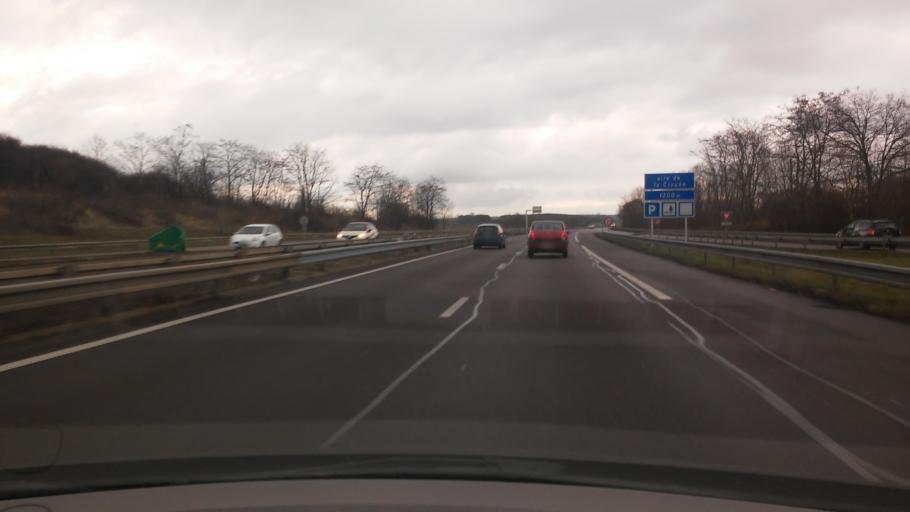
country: FR
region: Lorraine
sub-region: Departement de la Moselle
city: Argancy
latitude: 49.1966
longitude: 6.2111
